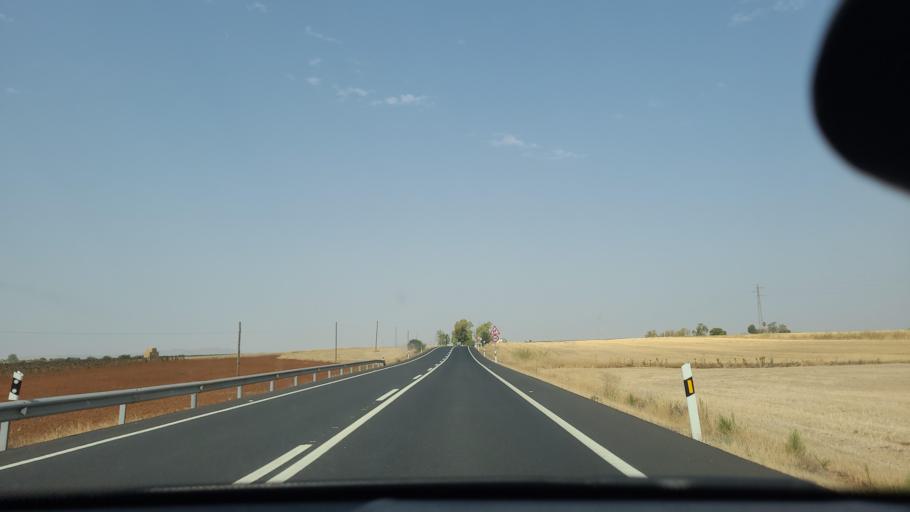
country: ES
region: Extremadura
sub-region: Provincia de Badajoz
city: Berlanga
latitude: 38.2655
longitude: -5.7579
